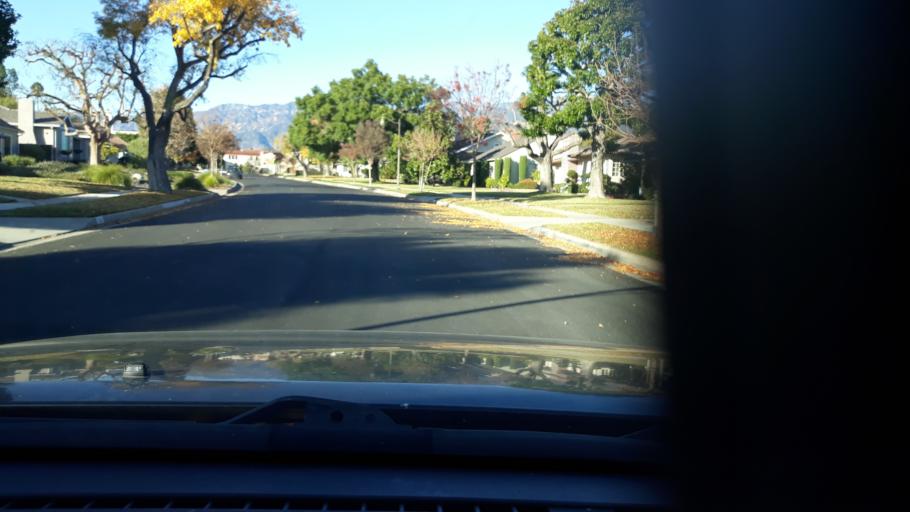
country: US
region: California
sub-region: Los Angeles County
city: San Marino
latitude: 34.1242
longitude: -118.0915
